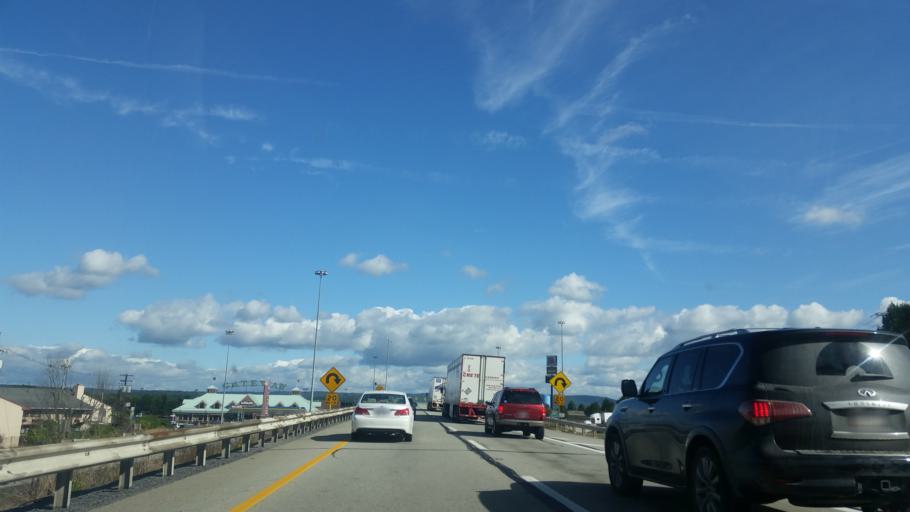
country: US
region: Pennsylvania
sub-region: Bedford County
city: Earlston
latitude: 39.9975
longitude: -78.2333
